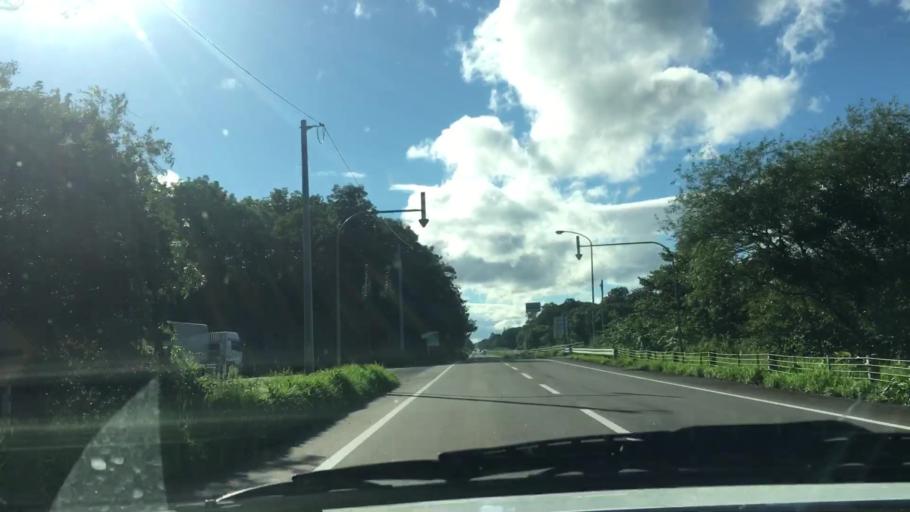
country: JP
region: Hokkaido
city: Otofuke
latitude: 43.1665
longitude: 143.1316
